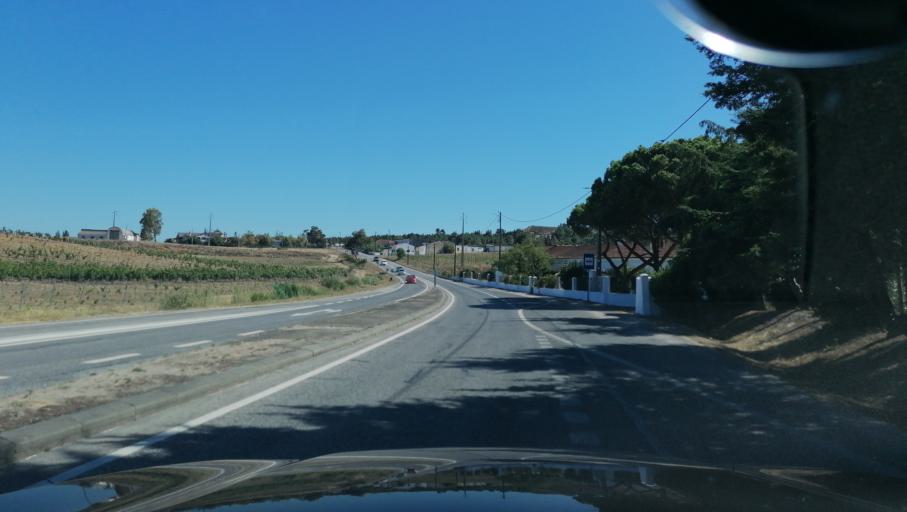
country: PT
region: Lisbon
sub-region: Azambuja
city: Alcoentre
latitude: 39.1365
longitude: -8.9980
